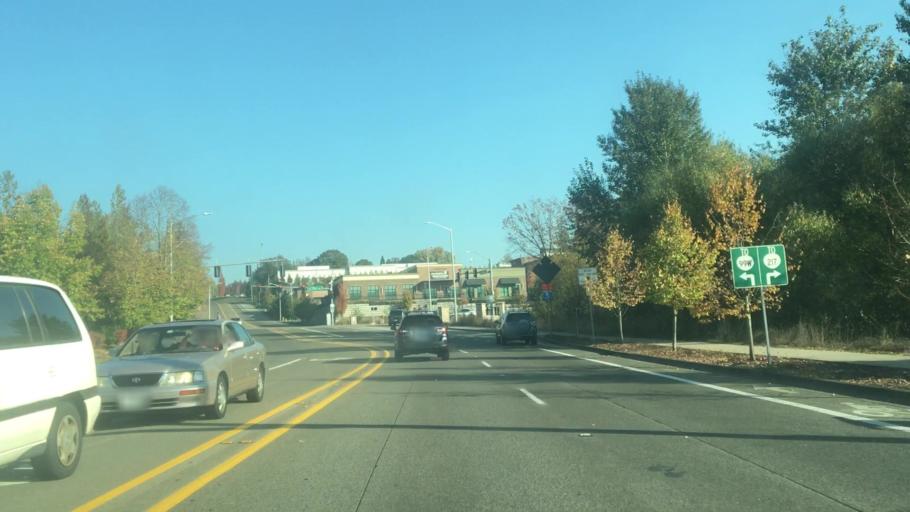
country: US
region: Oregon
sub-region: Washington County
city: Metzger
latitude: 45.4332
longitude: -122.7527
